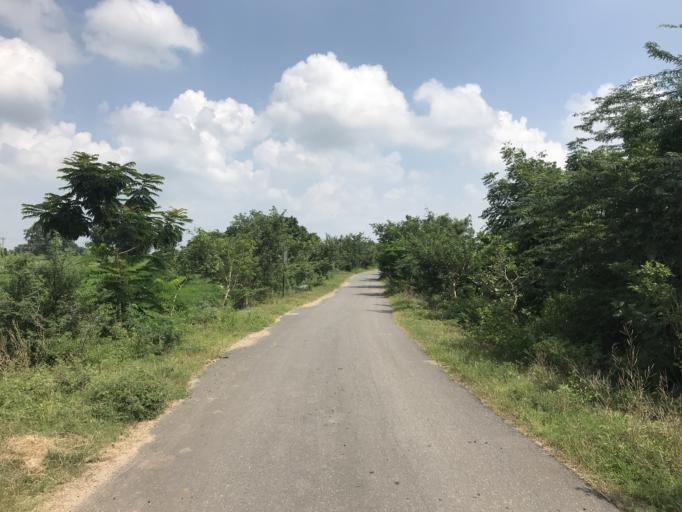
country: IN
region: Telangana
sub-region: Warangal
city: Mahbubabad
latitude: 17.6859
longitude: 79.7159
